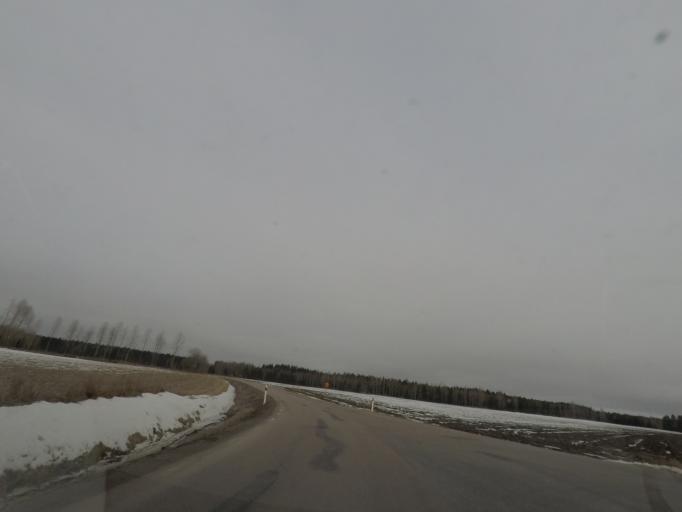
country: SE
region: Vaestmanland
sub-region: Vasteras
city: Skultuna
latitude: 59.7366
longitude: 16.4122
